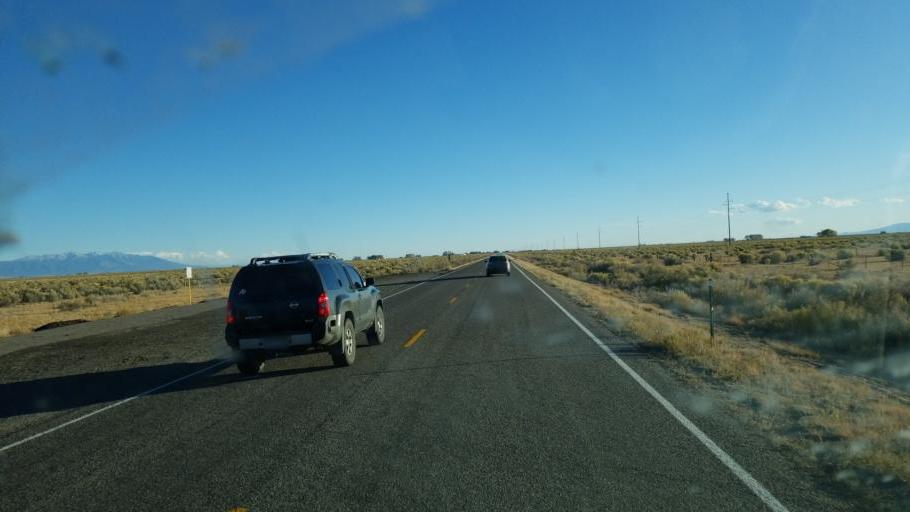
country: US
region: Colorado
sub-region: Saguache County
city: Saguache
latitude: 38.0649
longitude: -105.9158
